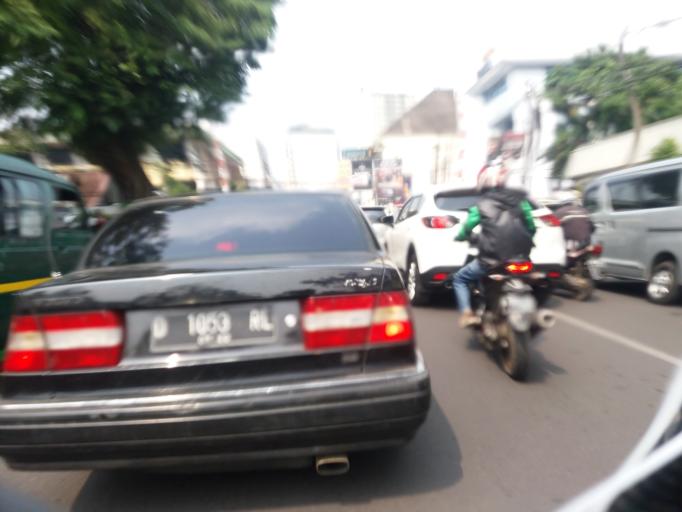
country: ID
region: West Java
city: Bandung
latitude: -6.9148
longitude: 107.6090
